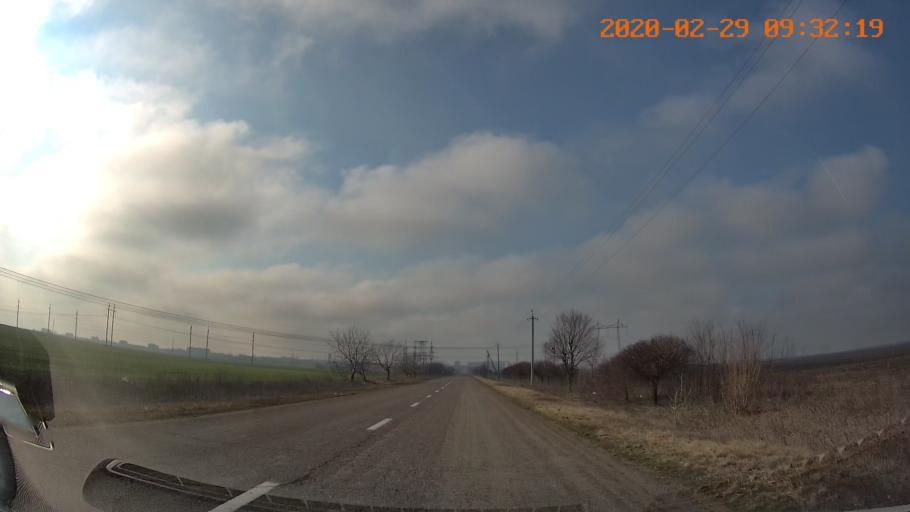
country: MD
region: Telenesti
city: Dnestrovsc
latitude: 46.6410
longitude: 29.9066
